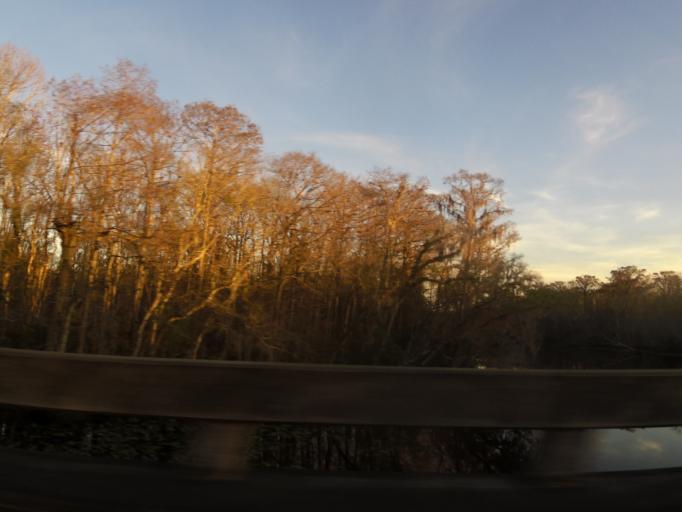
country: US
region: Florida
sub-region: Clay County
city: Green Cove Springs
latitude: 29.9593
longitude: -81.5438
